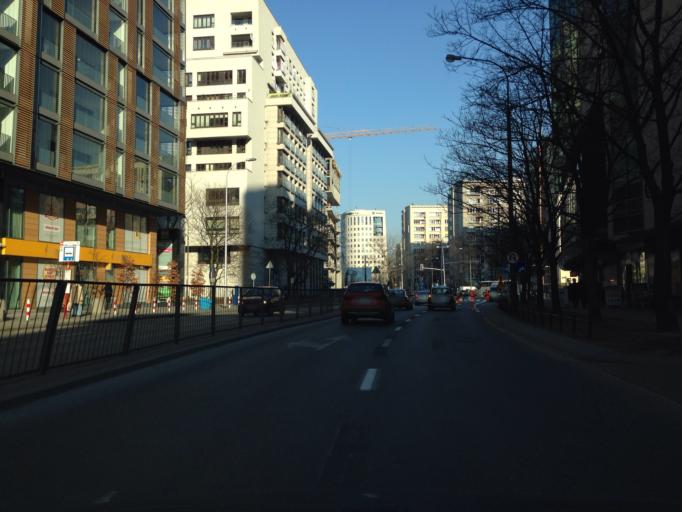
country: PL
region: Masovian Voivodeship
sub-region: Warszawa
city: Warsaw
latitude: 52.2372
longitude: 21.0014
